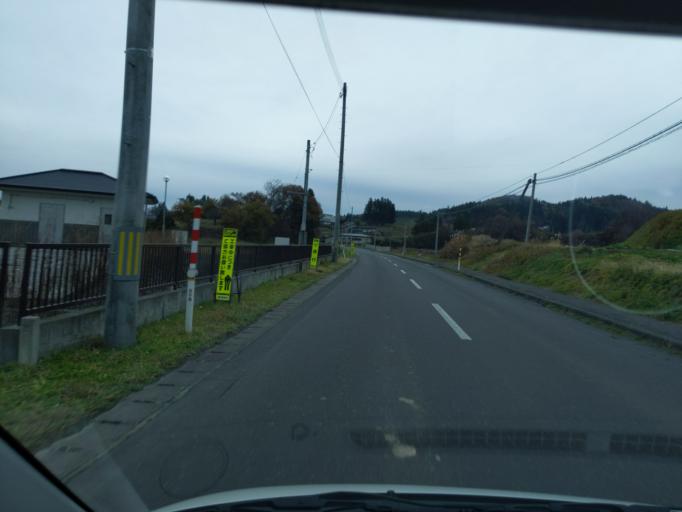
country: JP
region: Iwate
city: Kitakami
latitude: 39.2800
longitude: 141.2662
